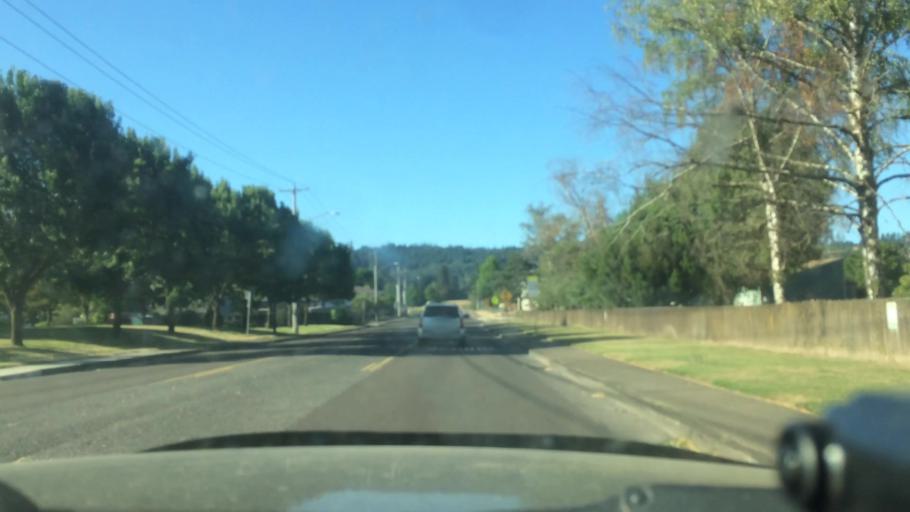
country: US
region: Oregon
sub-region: Yamhill County
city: Newberg
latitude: 45.3114
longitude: -122.9466
